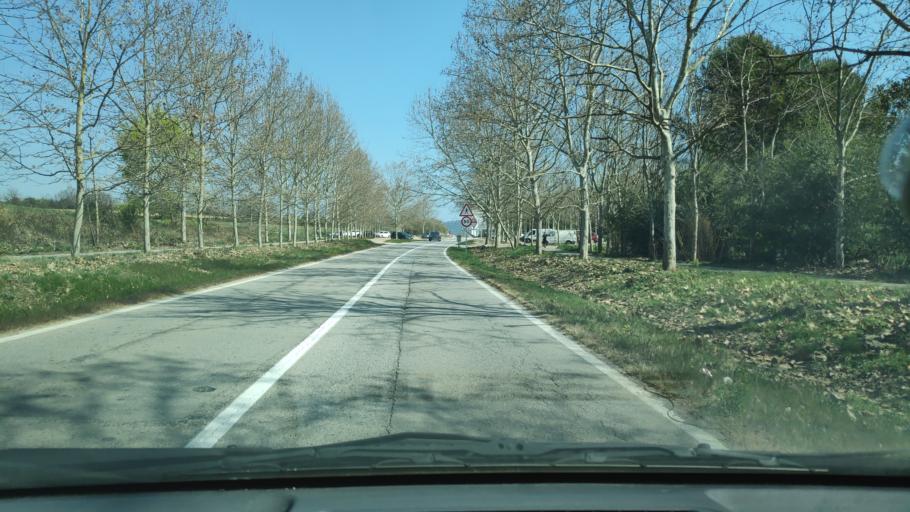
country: ES
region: Catalonia
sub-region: Provincia de Barcelona
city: Mollet del Valles
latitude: 41.5372
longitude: 2.1985
